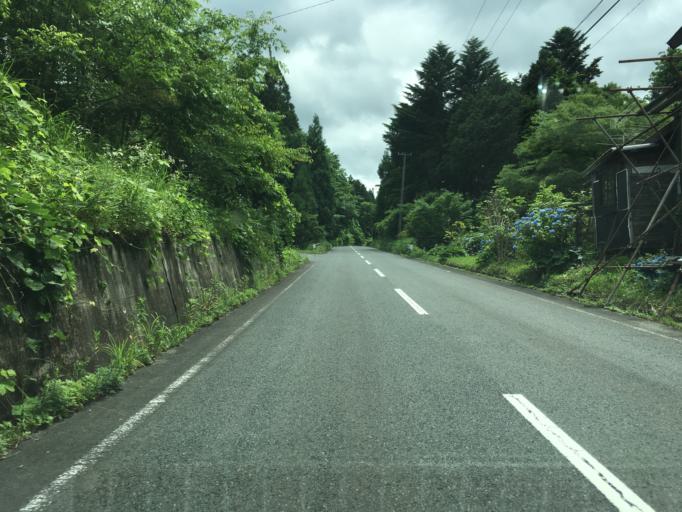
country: JP
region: Miyagi
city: Marumori
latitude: 37.7164
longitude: 140.8849
